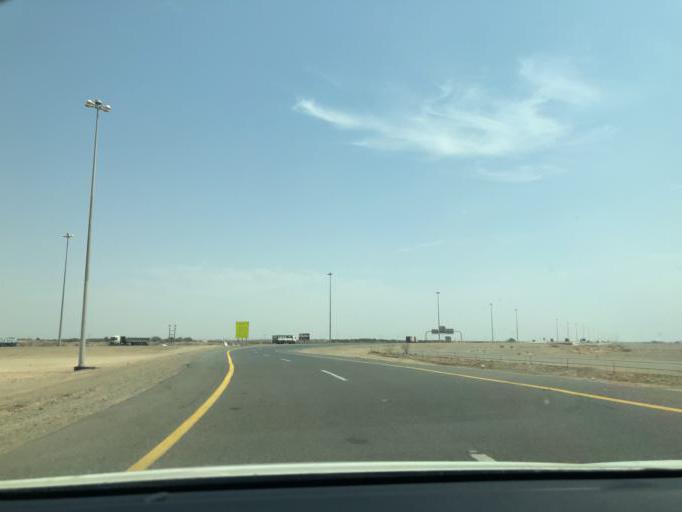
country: SA
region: Makkah
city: Rabigh
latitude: 22.2732
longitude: 39.1240
